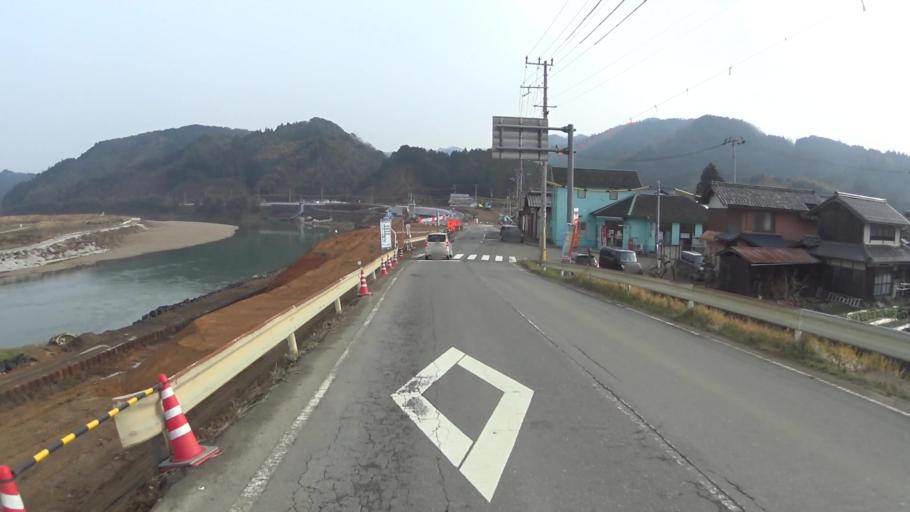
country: JP
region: Kyoto
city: Fukuchiyama
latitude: 35.3889
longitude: 135.1801
